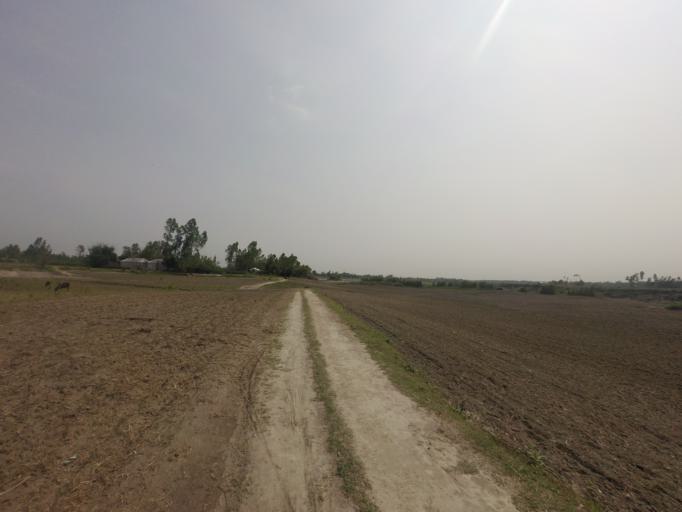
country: BD
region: Rajshahi
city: Sirajganj
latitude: 24.3497
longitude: 89.7279
